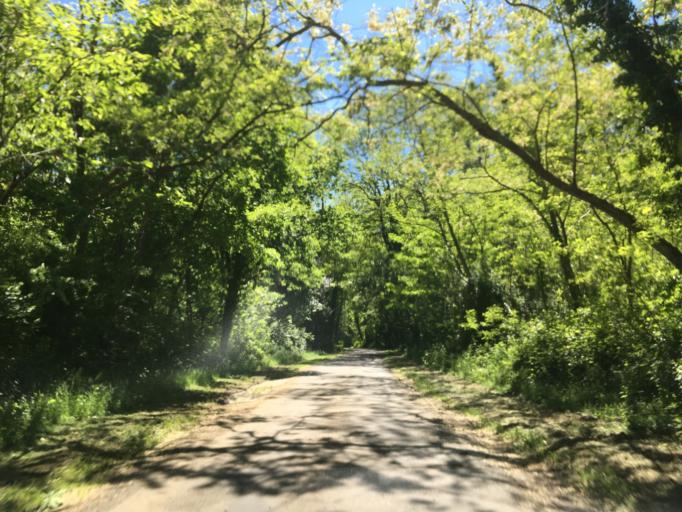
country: FR
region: Aquitaine
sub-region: Departement de la Gironde
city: Lesparre-Medoc
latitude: 45.2911
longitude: -0.8948
